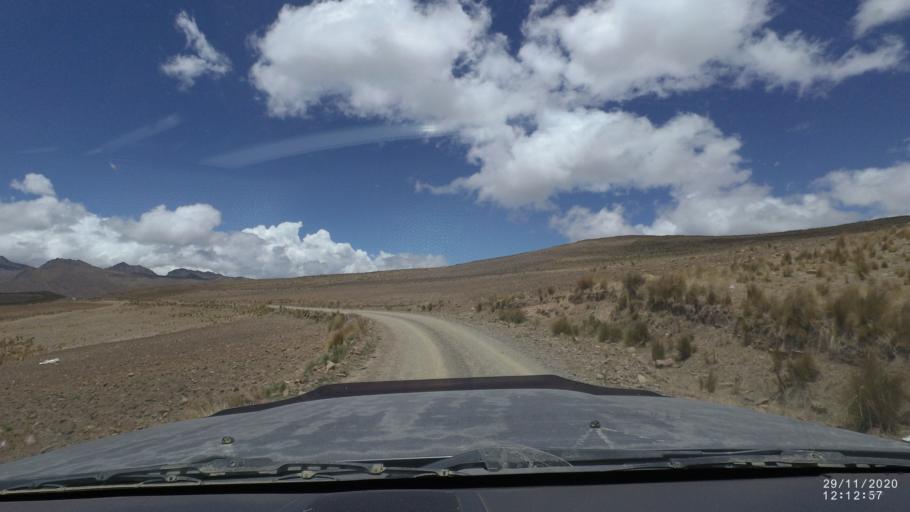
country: BO
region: Cochabamba
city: Cochabamba
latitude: -17.1101
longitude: -66.3040
